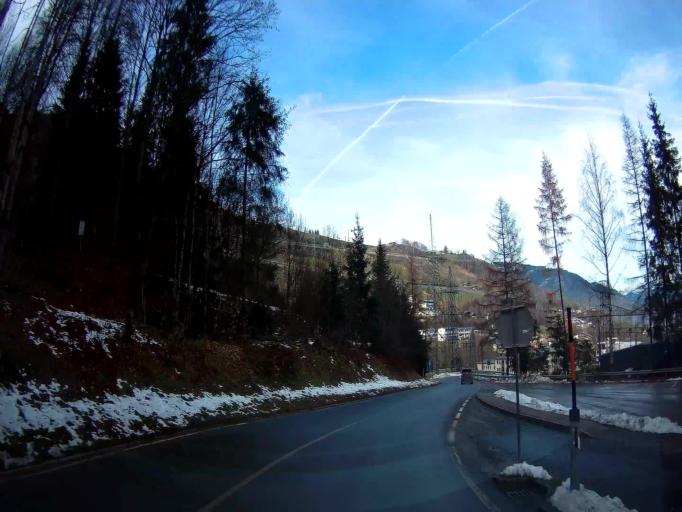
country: AT
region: Salzburg
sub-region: Politischer Bezirk Zell am See
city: Kaprun
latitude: 47.2578
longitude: 12.7407
